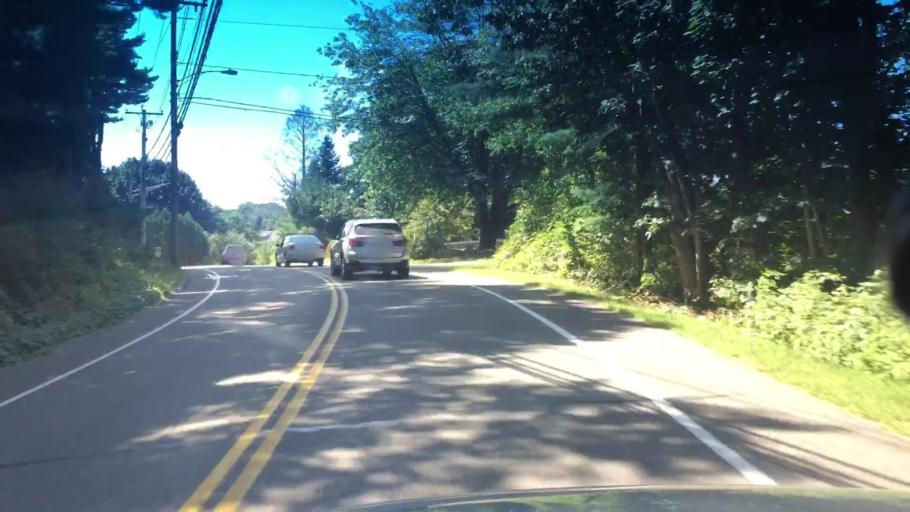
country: US
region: Maine
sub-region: York County
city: York Beach
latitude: 43.1625
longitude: -70.6275
